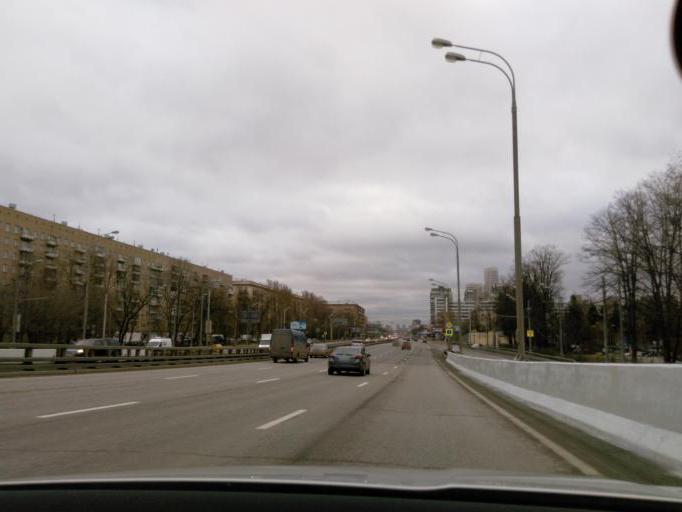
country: RU
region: Moskovskaya
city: Levoberezhnyy
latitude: 55.8378
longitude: 37.4823
